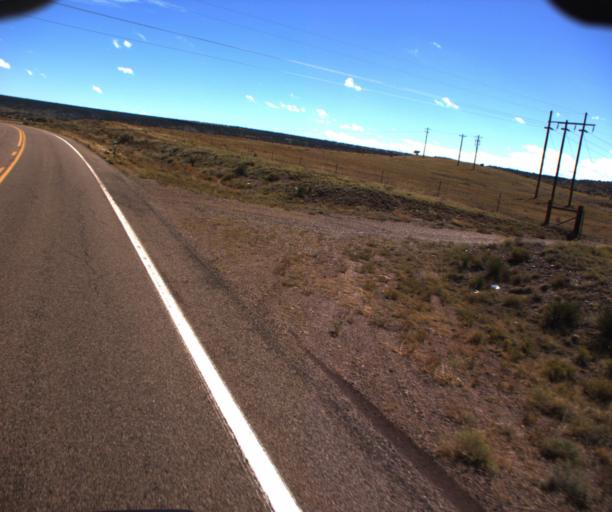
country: US
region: Arizona
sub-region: Apache County
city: Saint Johns
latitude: 34.4824
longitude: -109.6185
